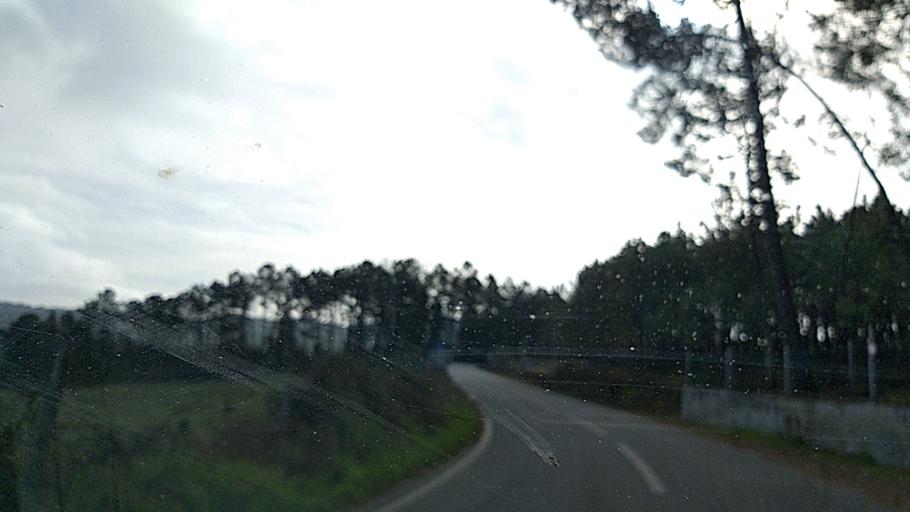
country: PT
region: Guarda
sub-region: Fornos de Algodres
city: Fornos de Algodres
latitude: 40.6994
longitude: -7.5616
